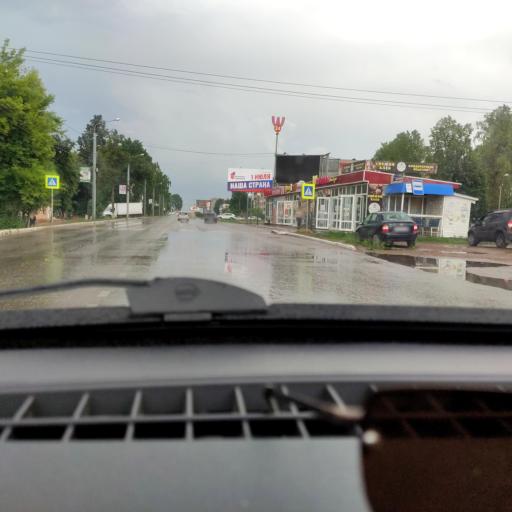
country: RU
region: Bashkortostan
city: Birsk
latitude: 55.4148
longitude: 55.5525
